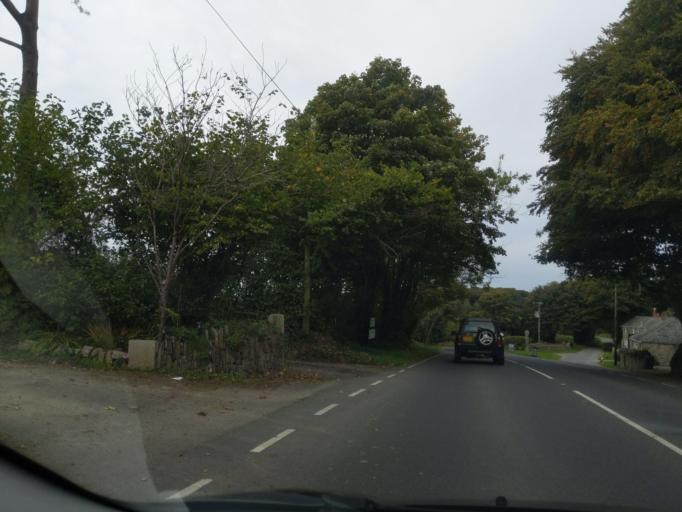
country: GB
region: England
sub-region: Cornwall
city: Bodmin
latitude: 50.4940
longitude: -4.7680
